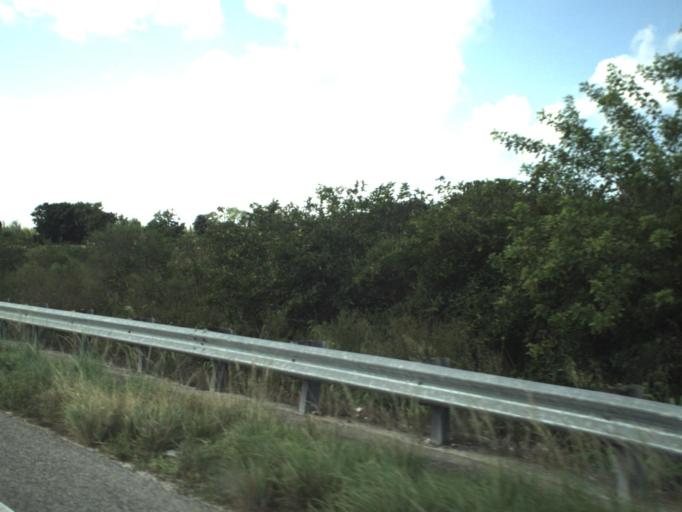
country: US
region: Florida
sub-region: Broward County
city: Weston
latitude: 26.0628
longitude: -80.4345
